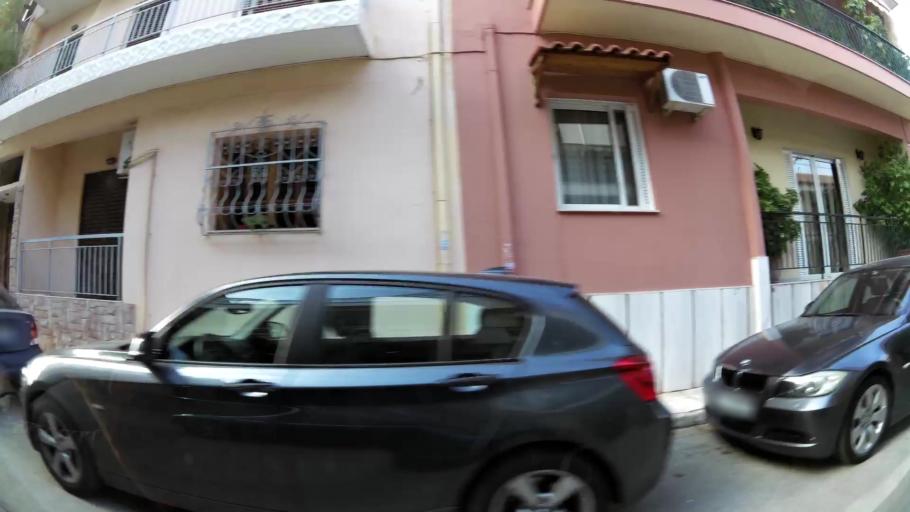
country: GR
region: Attica
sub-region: Nomarchia Athinas
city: Ilion
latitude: 38.0392
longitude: 23.6981
